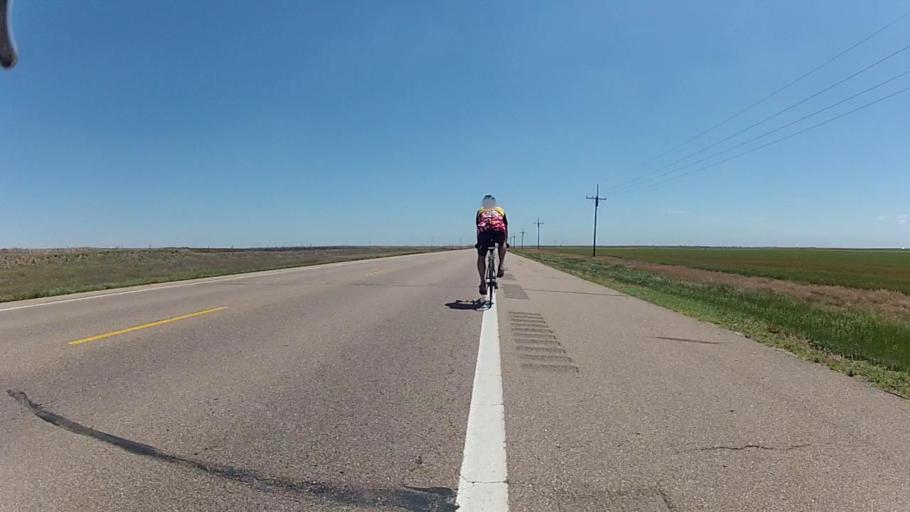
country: US
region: Kansas
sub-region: Ford County
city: Dodge City
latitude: 37.7119
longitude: -100.1115
